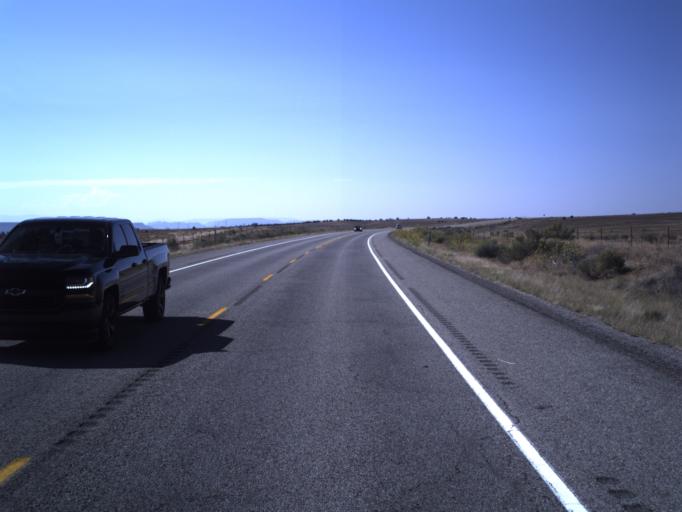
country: US
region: Utah
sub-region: San Juan County
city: Blanding
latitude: 37.4487
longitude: -109.4671
